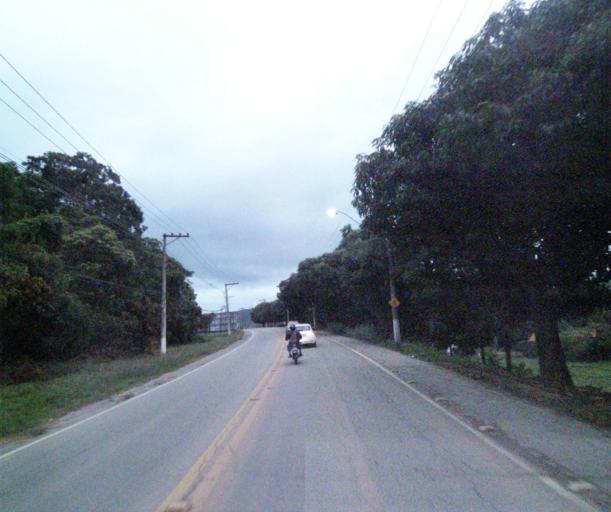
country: BR
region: Espirito Santo
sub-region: Castelo
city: Castelo
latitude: -20.6271
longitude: -41.2024
